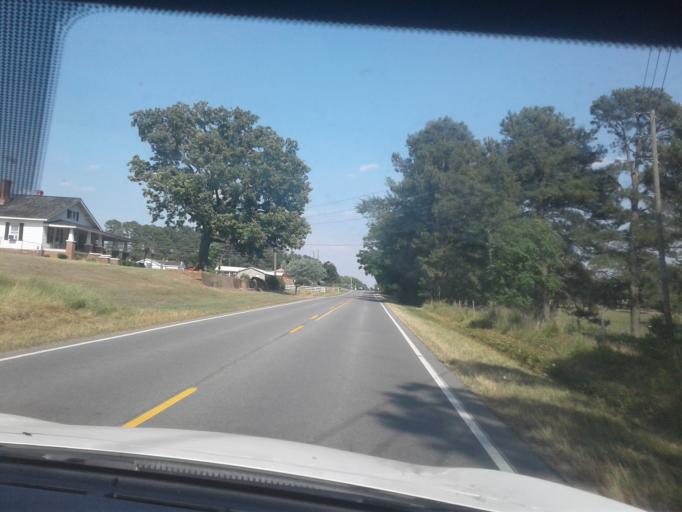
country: US
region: North Carolina
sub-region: Johnston County
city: Benson
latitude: 35.3885
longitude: -78.5693
